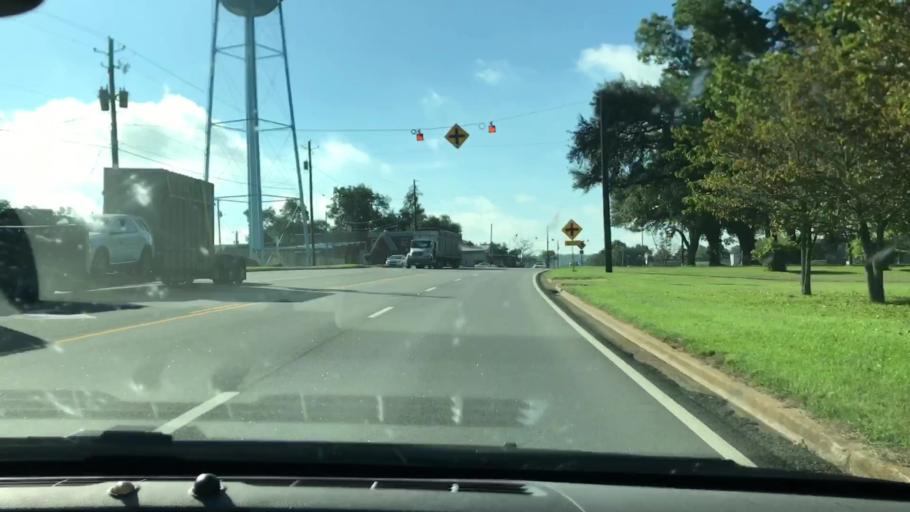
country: US
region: Georgia
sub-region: Terrell County
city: Dawson
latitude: 31.7207
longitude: -84.3496
